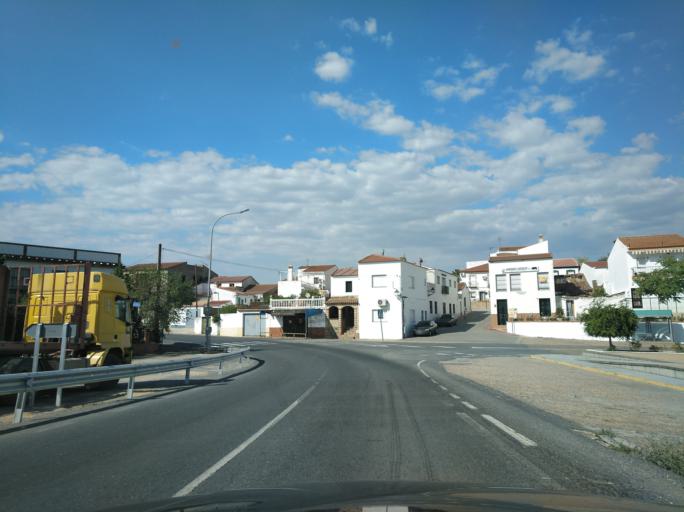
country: ES
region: Andalusia
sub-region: Provincia de Huelva
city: Cabezas Rubias
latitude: 37.7270
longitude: -7.0890
